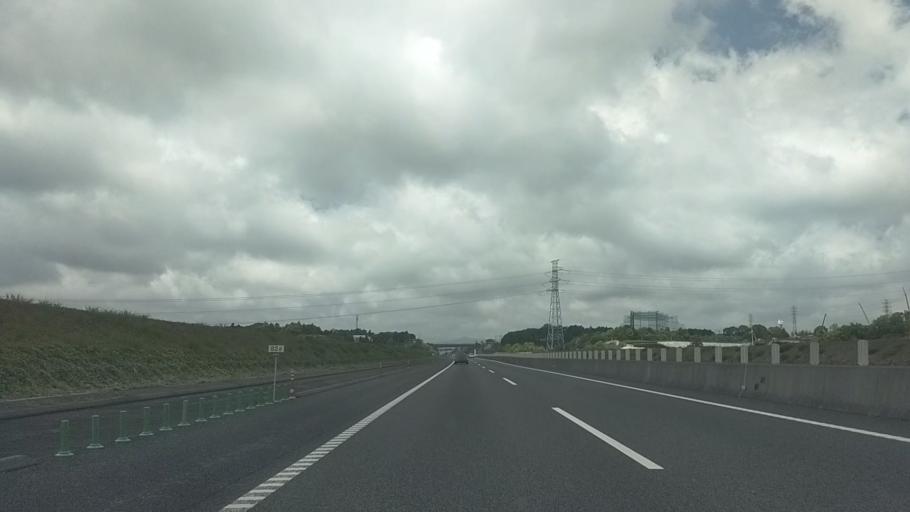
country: JP
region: Shizuoka
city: Fuji
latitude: 35.1945
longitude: 138.7045
